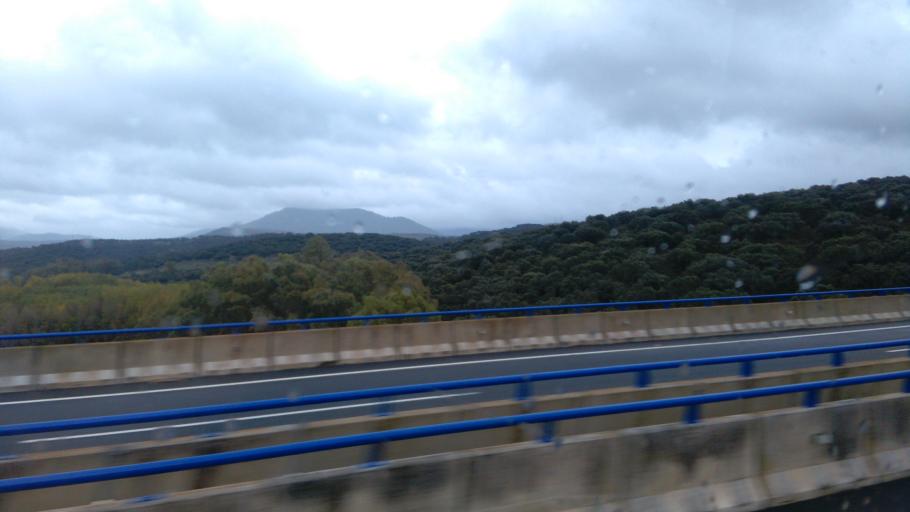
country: ES
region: Extremadura
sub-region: Provincia de Caceres
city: Romangordo
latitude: 39.7797
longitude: -5.7331
